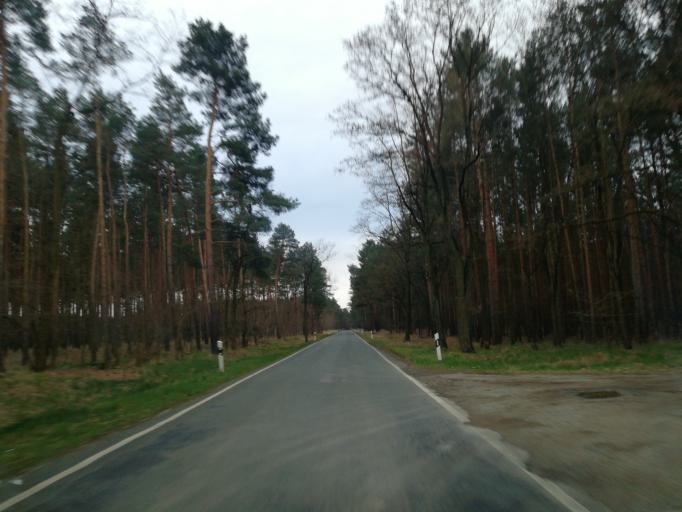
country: DE
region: Brandenburg
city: Vetschau
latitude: 51.7505
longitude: 14.1319
